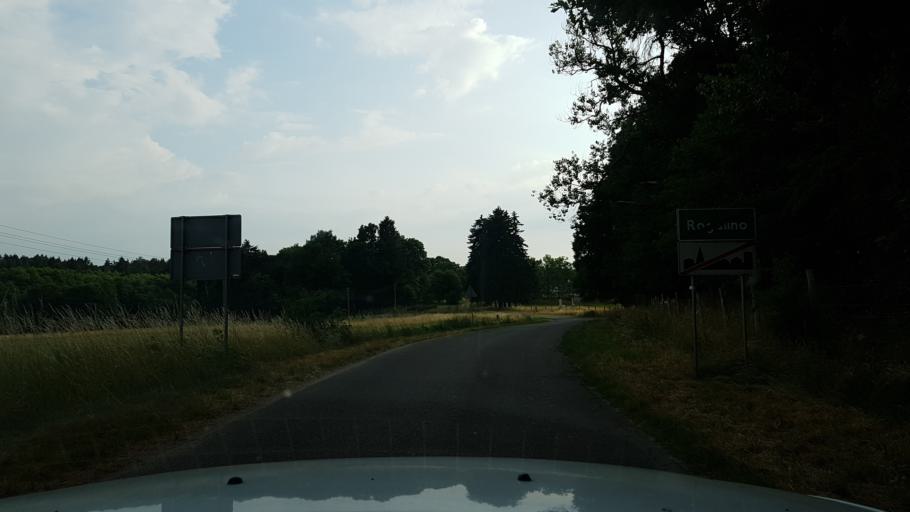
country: PL
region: West Pomeranian Voivodeship
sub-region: Powiat swidwinski
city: Swidwin
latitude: 53.8067
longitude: 15.8418
